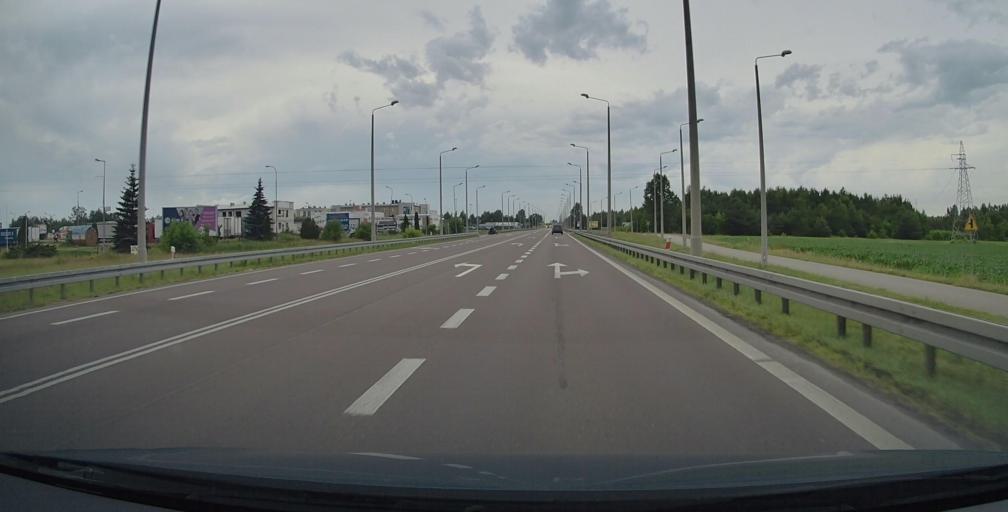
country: PL
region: Lublin Voivodeship
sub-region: Biala Podlaska
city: Biala Podlaska
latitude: 52.0456
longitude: 23.1526
